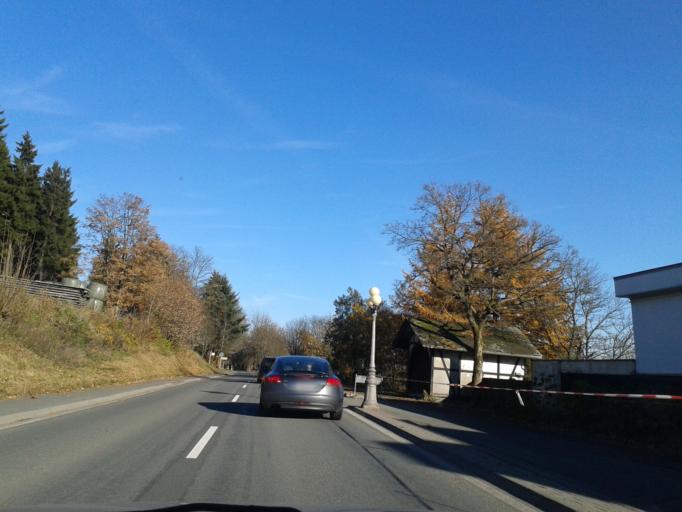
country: DE
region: North Rhine-Westphalia
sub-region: Regierungsbezirk Arnsberg
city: Winterberg
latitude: 51.1431
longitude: 8.4460
